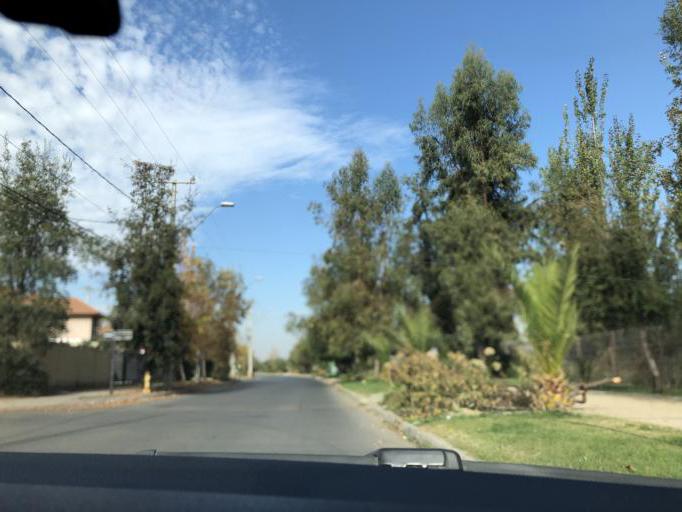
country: CL
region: Santiago Metropolitan
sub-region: Provincia de Cordillera
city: Puente Alto
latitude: -33.5756
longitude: -70.5430
